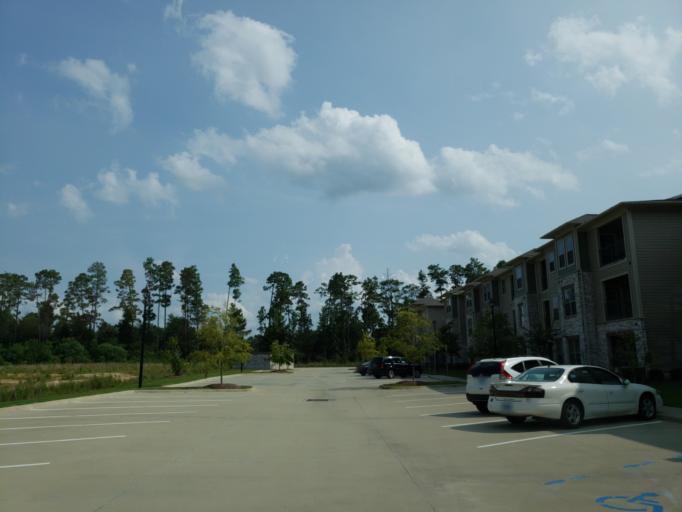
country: US
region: Mississippi
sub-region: Forrest County
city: Hattiesburg
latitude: 31.2767
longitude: -89.3219
